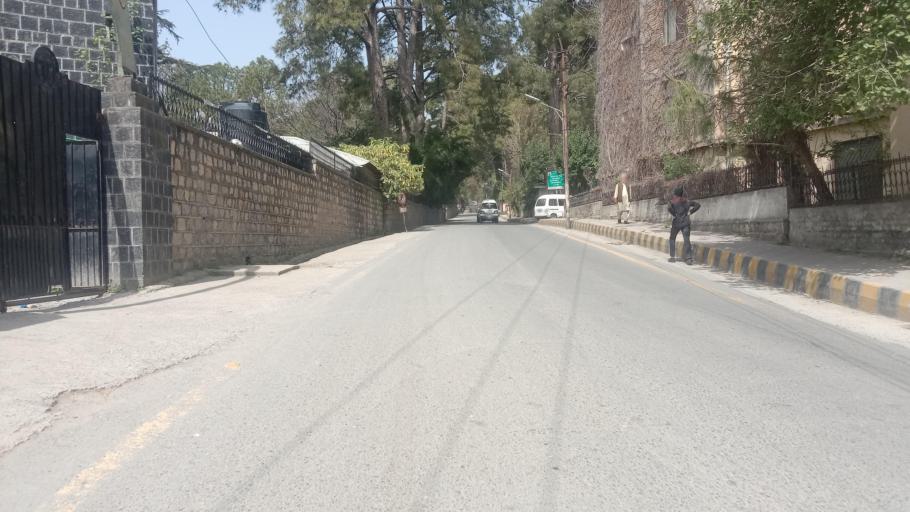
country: PK
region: Khyber Pakhtunkhwa
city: Abbottabad
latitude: 34.1434
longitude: 73.2102
